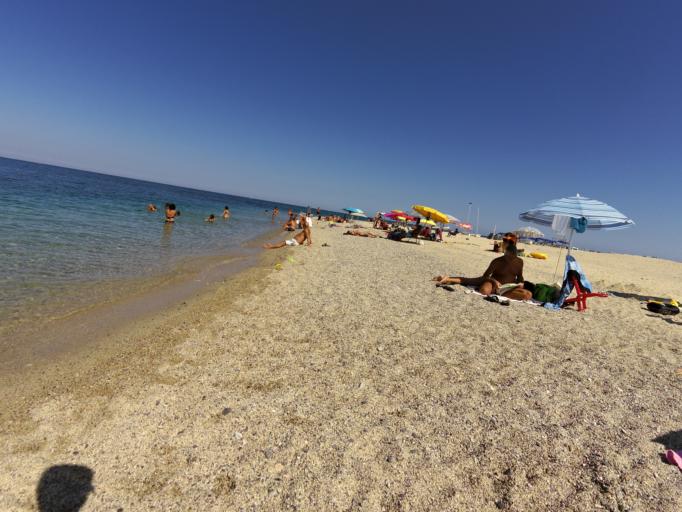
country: IT
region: Calabria
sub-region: Provincia di Catanzaro
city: Soverato Marina
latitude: 38.6918
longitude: 16.5534
